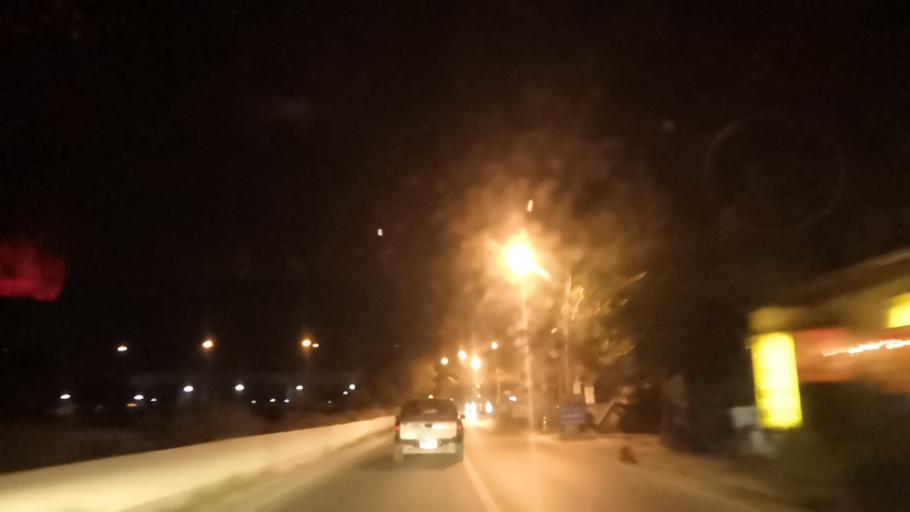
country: TH
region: Chiang Mai
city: Saraphi
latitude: 18.7218
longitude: 98.9861
